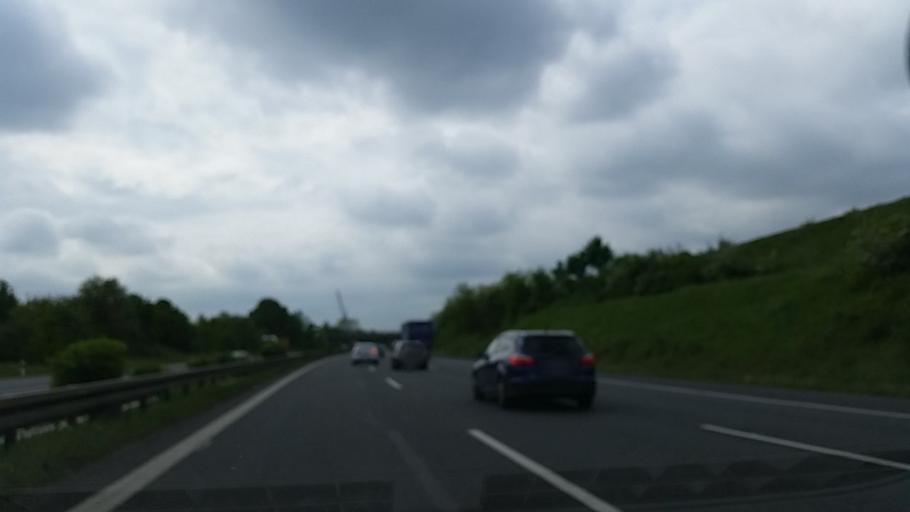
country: DE
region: Brandenburg
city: Schulzendorf
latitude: 52.3467
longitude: 13.5549
